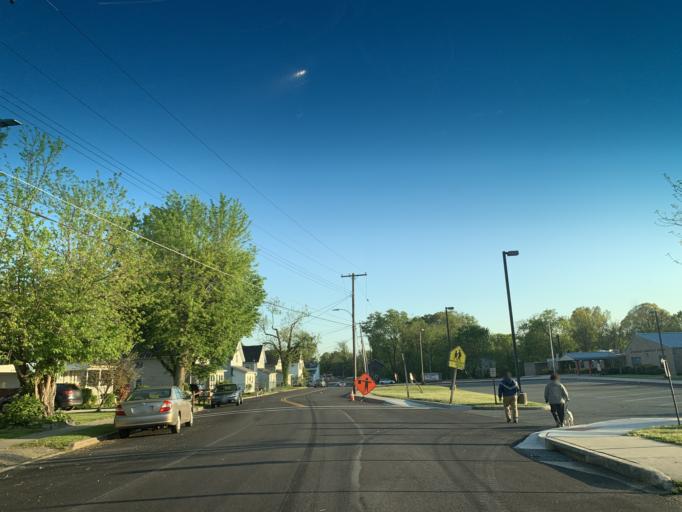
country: US
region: Maryland
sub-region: Harford County
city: Aberdeen
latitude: 39.5138
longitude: -76.1696
